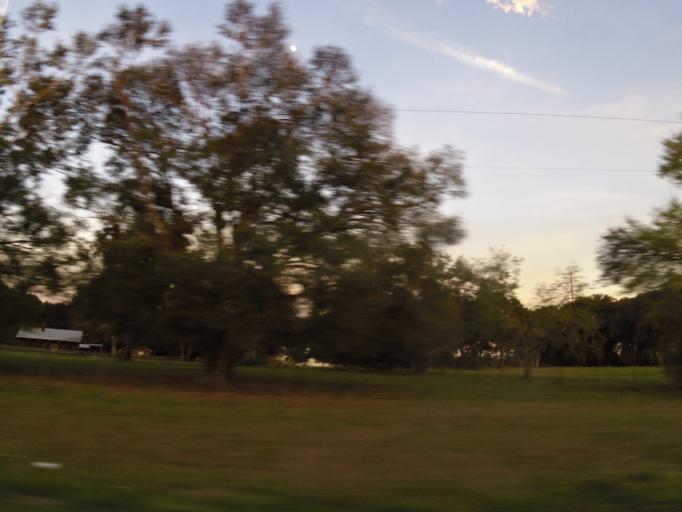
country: US
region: Florida
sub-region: Volusia County
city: De Leon Springs
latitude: 29.1300
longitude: -81.2852
